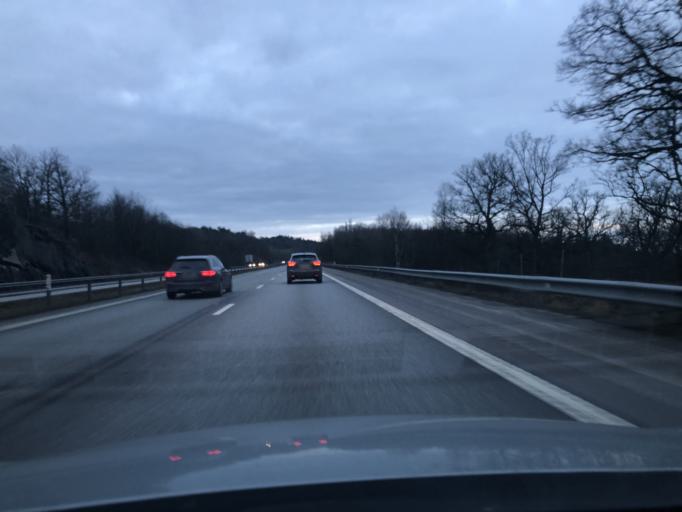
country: SE
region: Joenkoeping
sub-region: Jonkopings Kommun
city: Graenna
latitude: 58.0336
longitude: 14.4910
